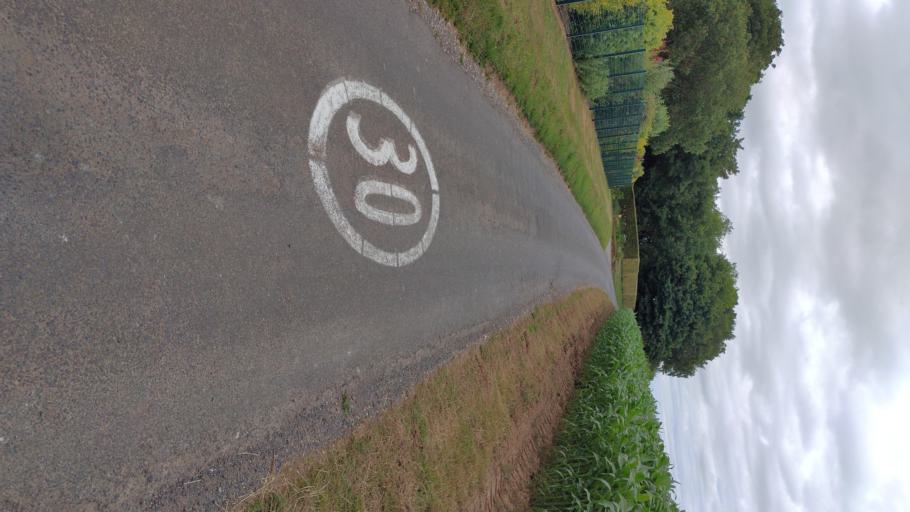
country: FR
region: Picardie
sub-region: Departement de la Somme
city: Ault
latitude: 50.0804
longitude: 1.4336
